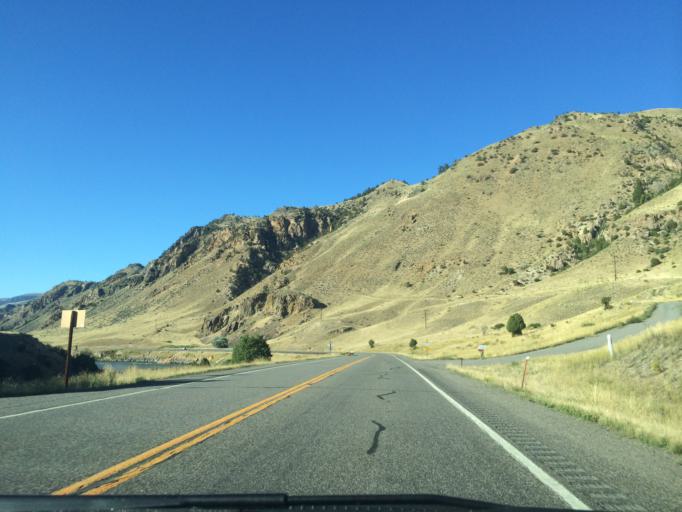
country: US
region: Montana
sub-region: Gallatin County
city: West Yellowstone
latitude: 45.0867
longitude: -110.7754
